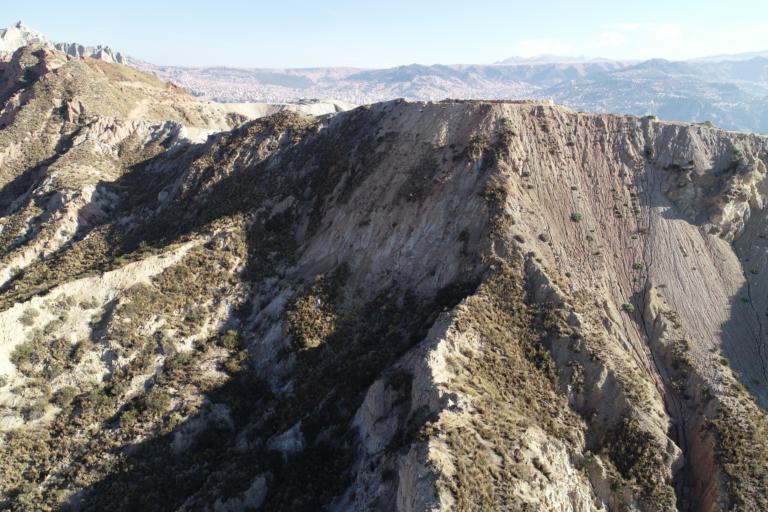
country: BO
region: La Paz
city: La Paz
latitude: -16.5509
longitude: -68.1077
